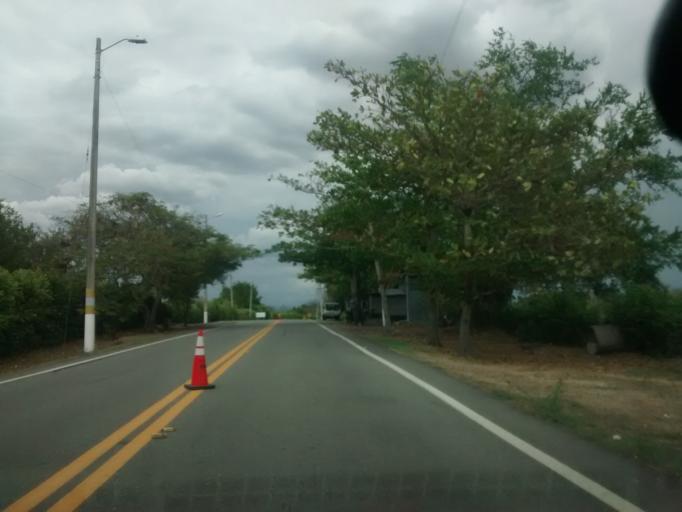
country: CO
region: Cundinamarca
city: Agua de Dios
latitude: 4.4089
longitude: -74.7161
